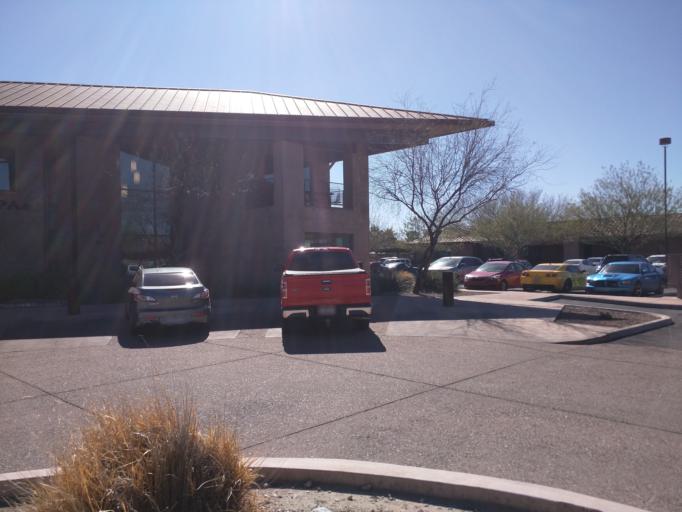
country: US
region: Arizona
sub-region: Pima County
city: Catalina Foothills
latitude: 32.2645
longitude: -110.8957
